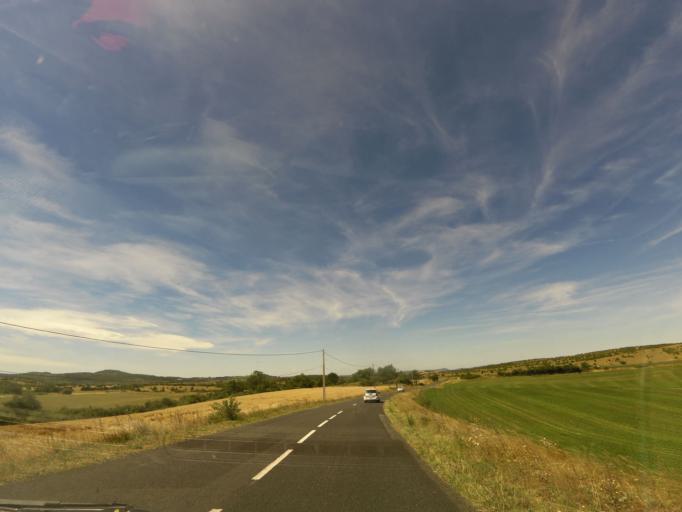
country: FR
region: Midi-Pyrenees
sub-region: Departement de l'Aveyron
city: La Cavalerie
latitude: 43.9639
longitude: 3.3221
